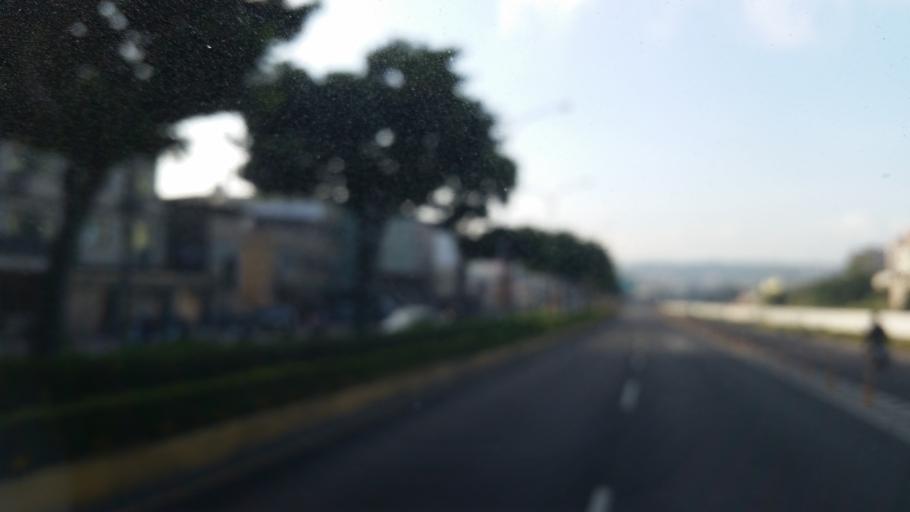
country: TW
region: Taiwan
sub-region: Taoyuan
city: Taoyuan
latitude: 25.0054
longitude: 121.3442
